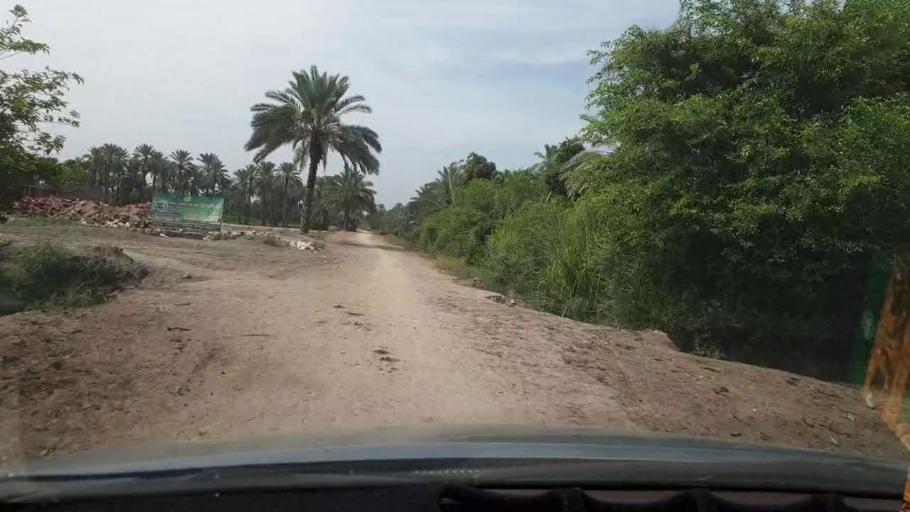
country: PK
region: Sindh
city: Khairpur
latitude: 27.5040
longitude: 68.7559
